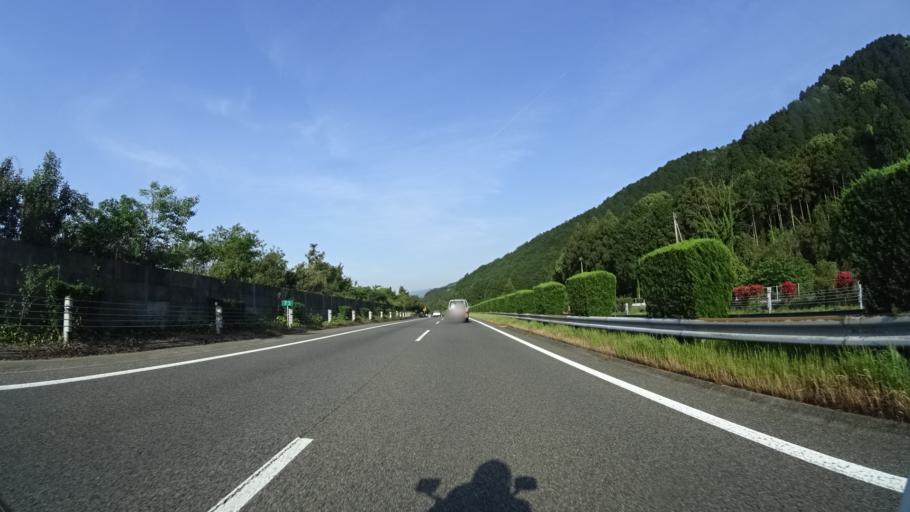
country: JP
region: Ehime
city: Niihama
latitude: 33.9525
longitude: 133.4434
